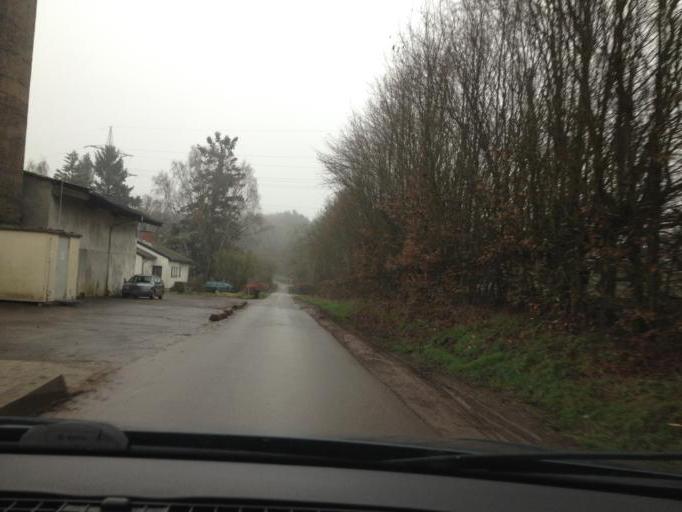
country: DE
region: Saarland
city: Marpingen
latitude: 49.4662
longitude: 7.0865
